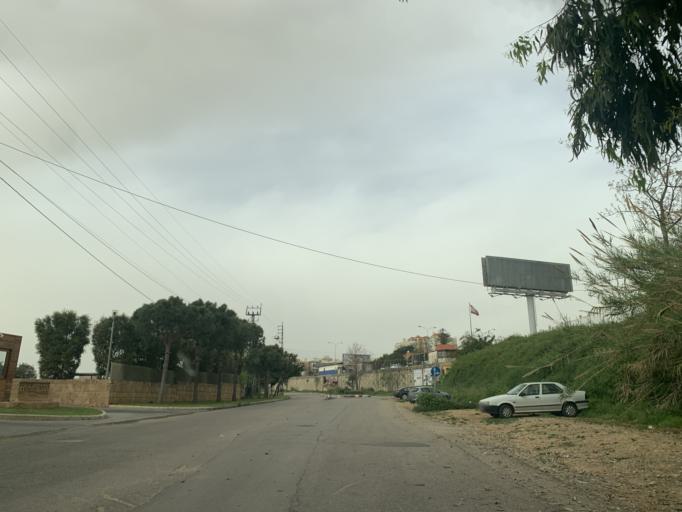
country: LB
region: Mont-Liban
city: Jbail
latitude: 34.1097
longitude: 35.6522
